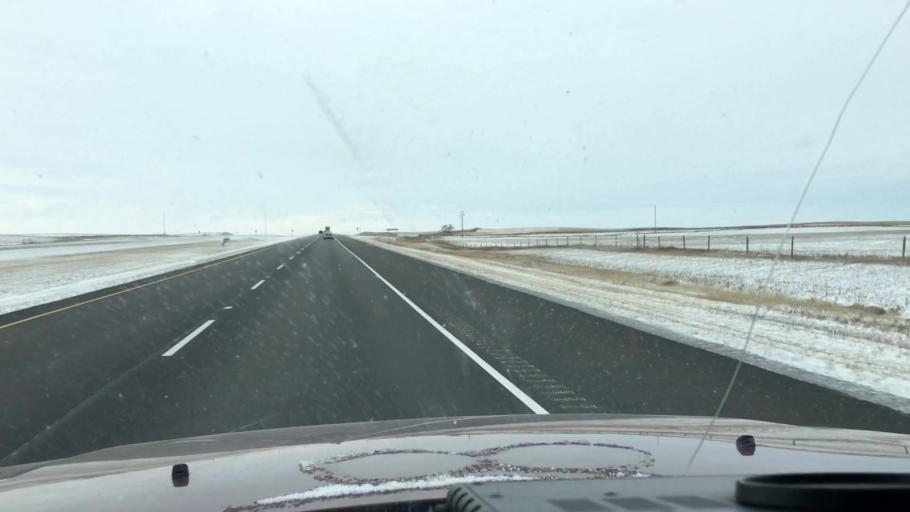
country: CA
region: Saskatchewan
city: Saskatoon
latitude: 51.7101
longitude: -106.4653
